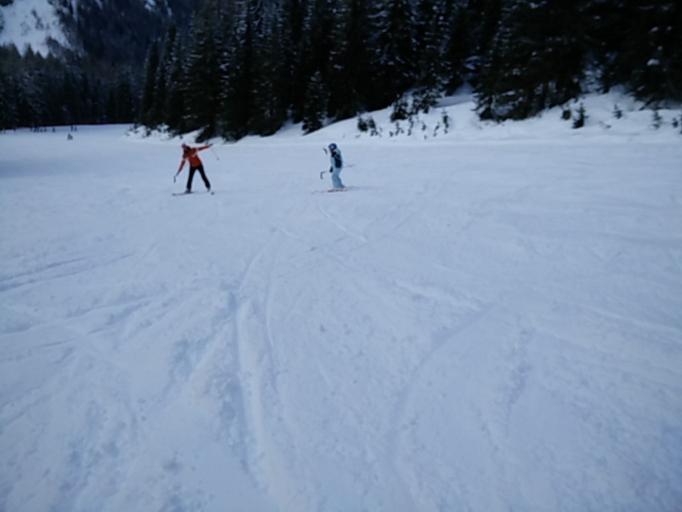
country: IT
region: Veneto
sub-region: Provincia di Belluno
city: Fusine
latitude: 46.3836
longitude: 12.0894
